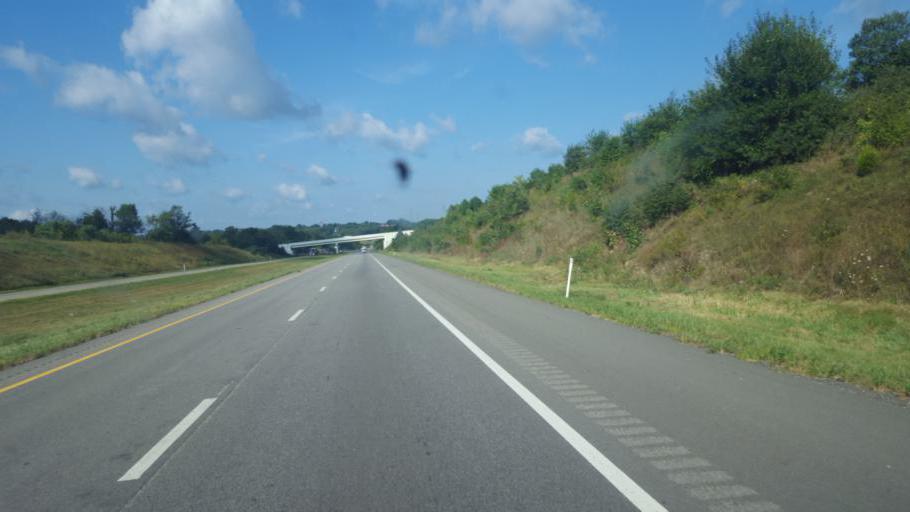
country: US
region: Ohio
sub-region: Wayne County
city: Smithville
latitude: 40.8025
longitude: -81.8732
